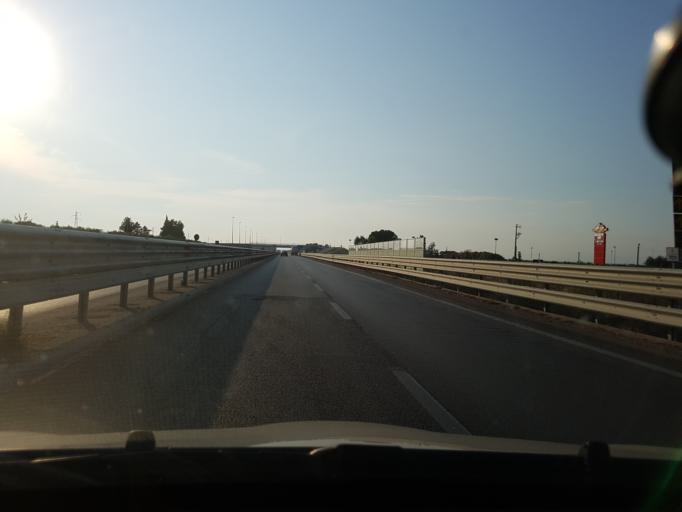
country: IT
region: Apulia
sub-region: Provincia di Foggia
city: Stornara
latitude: 41.3173
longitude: 15.7894
